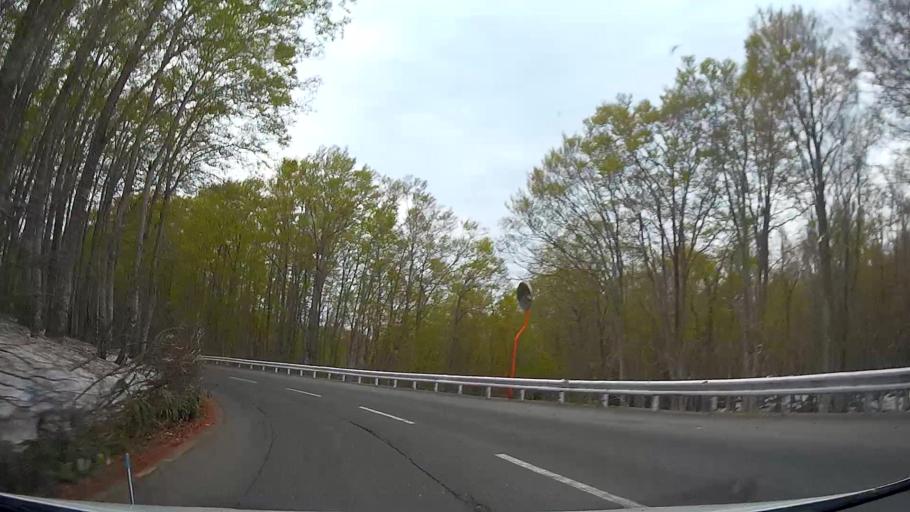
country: JP
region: Aomori
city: Aomori Shi
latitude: 40.6967
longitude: 140.8399
